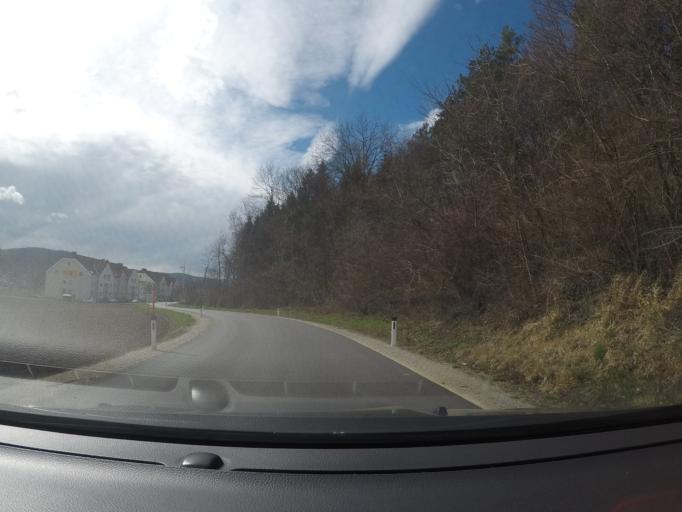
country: AT
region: Lower Austria
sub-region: Politischer Bezirk Neunkirchen
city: Pitten
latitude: 47.7279
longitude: 16.1930
